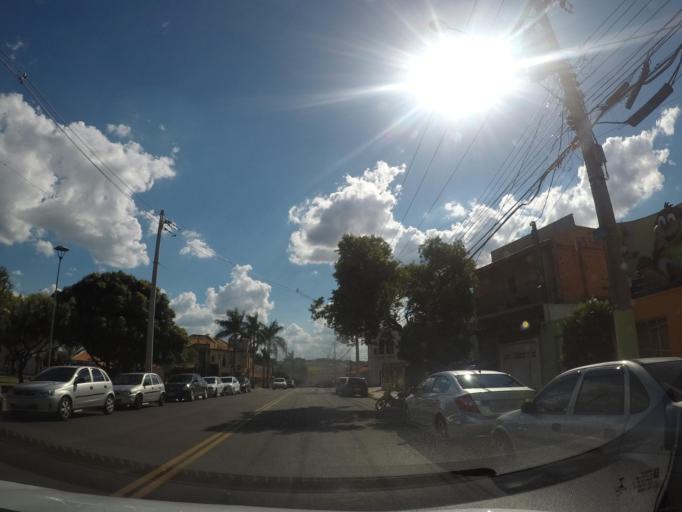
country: BR
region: Sao Paulo
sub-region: Sumare
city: Sumare
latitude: -22.8309
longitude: -47.2784
